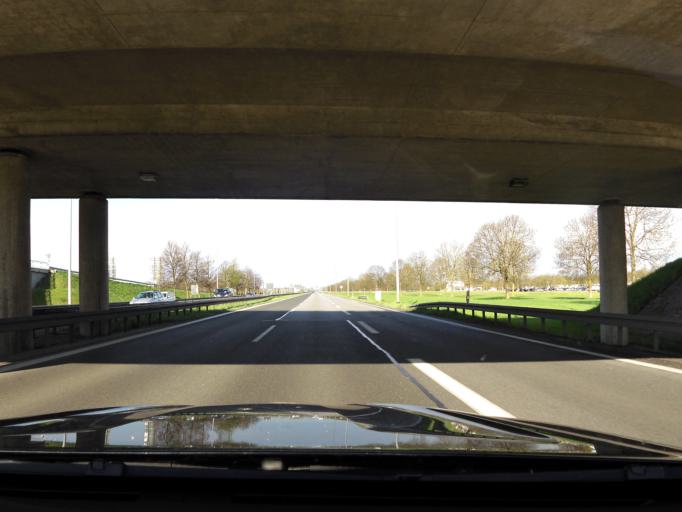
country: DE
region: Bavaria
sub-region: Upper Bavaria
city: Hallbergmoos
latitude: 48.3525
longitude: 11.7606
